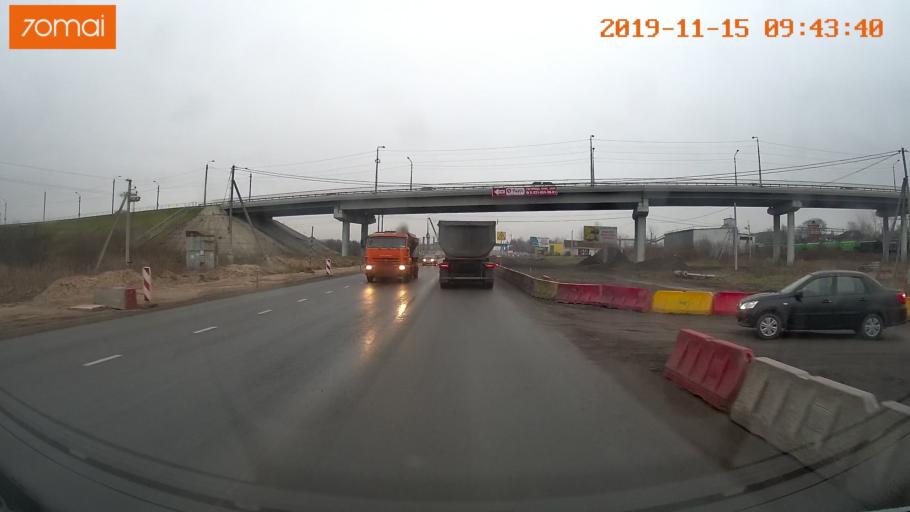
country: RU
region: Vologda
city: Sheksna
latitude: 59.2105
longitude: 38.5150
